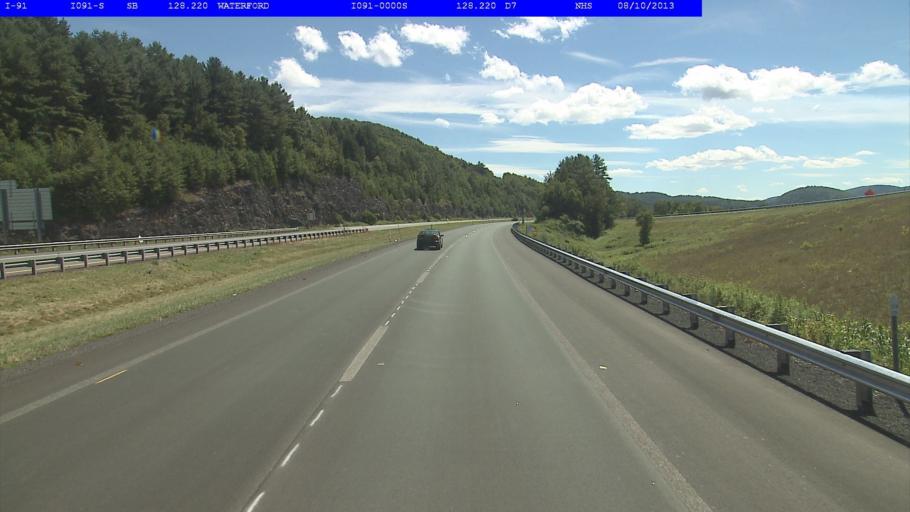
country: US
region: Vermont
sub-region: Caledonia County
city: Saint Johnsbury
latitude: 44.3961
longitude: -72.0178
